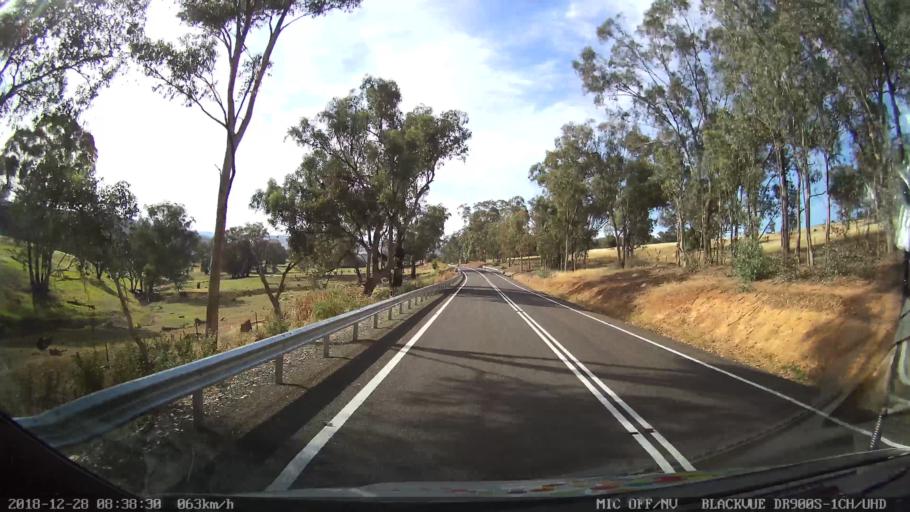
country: AU
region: New South Wales
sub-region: Blayney
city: Blayney
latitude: -34.0042
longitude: 149.3153
